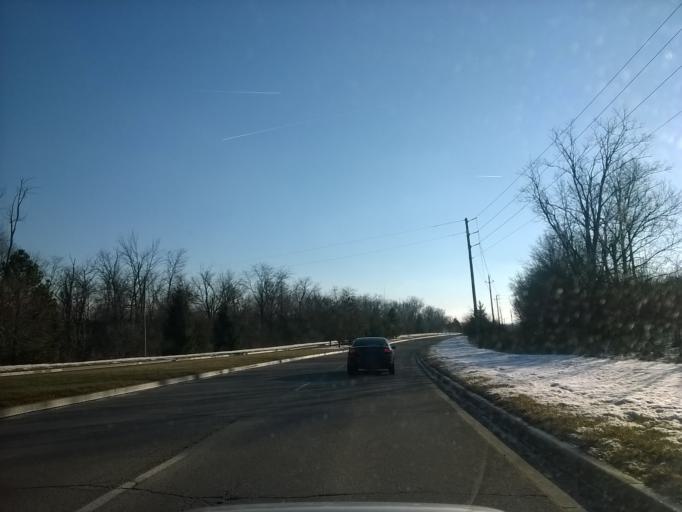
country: US
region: Indiana
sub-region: Hamilton County
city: Carmel
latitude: 39.9455
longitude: -86.0728
